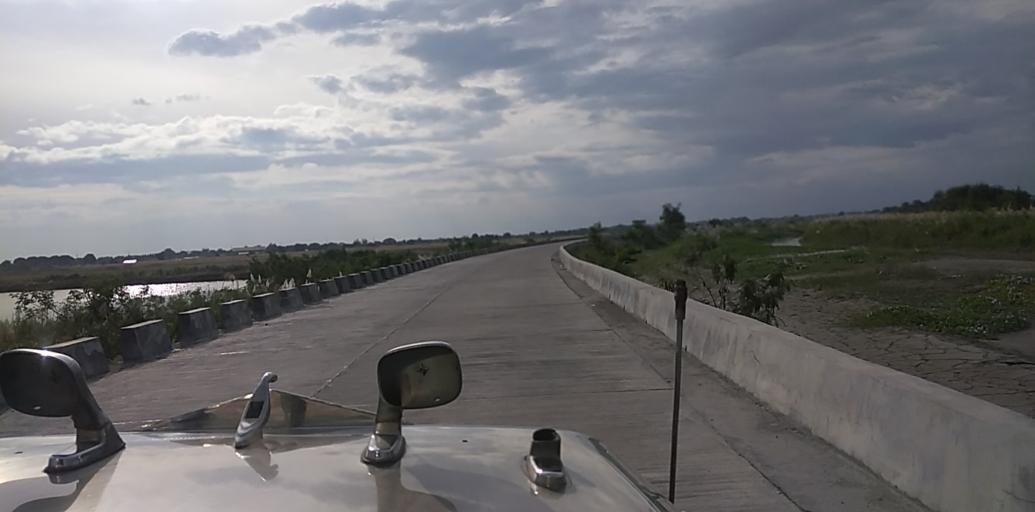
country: PH
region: Central Luzon
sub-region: Province of Pampanga
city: Minalin
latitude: 14.9671
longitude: 120.6703
